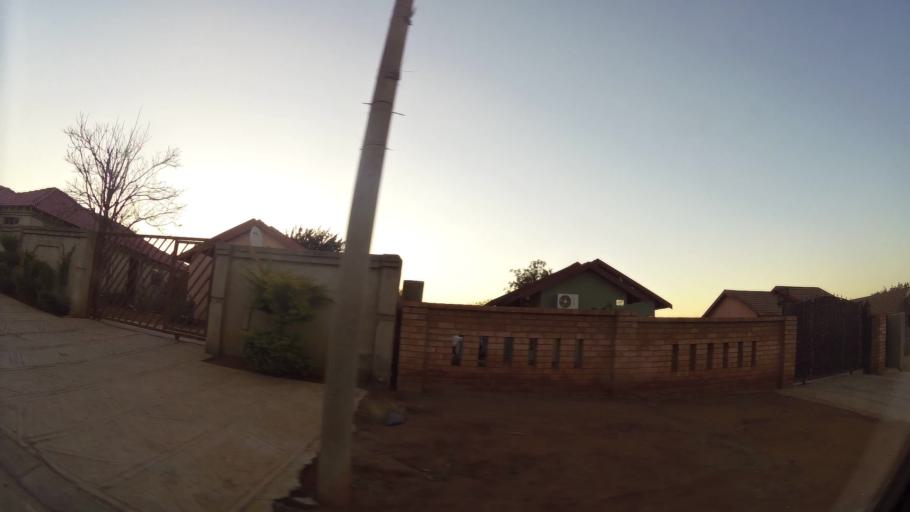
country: ZA
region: North-West
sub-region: Bojanala Platinum District Municipality
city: Rustenburg
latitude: -25.6499
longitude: 27.2088
